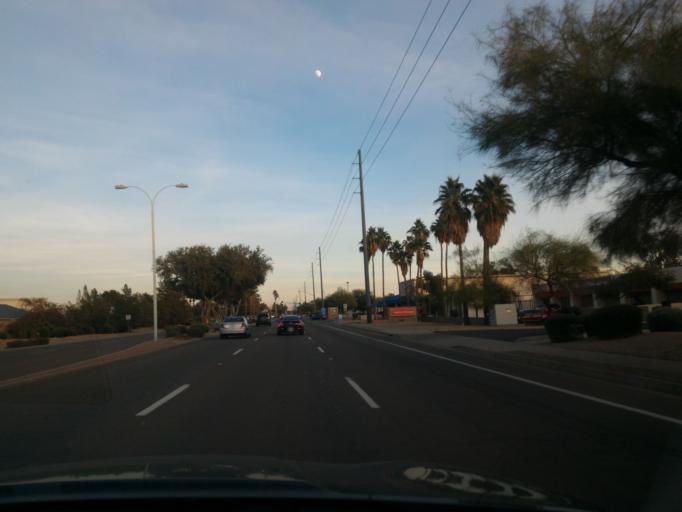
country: US
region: Arizona
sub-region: Maricopa County
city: Guadalupe
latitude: 33.3052
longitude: -111.9590
